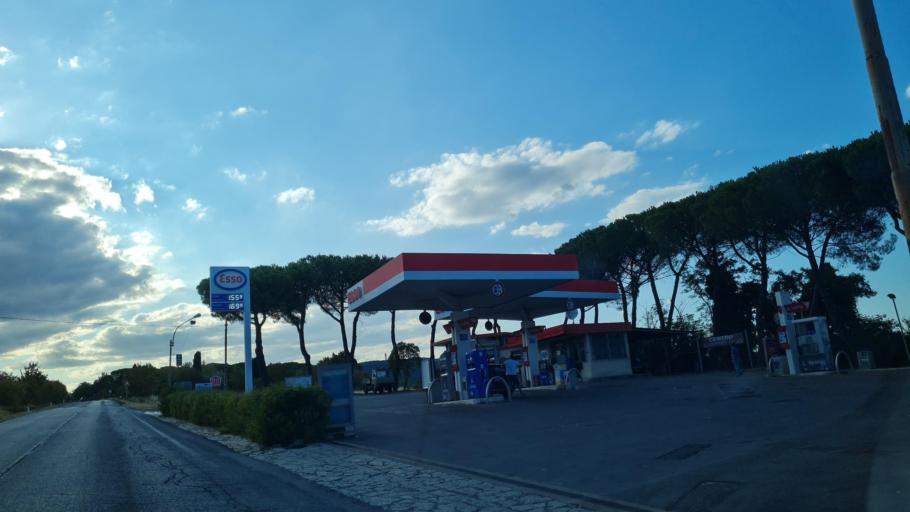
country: IT
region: Tuscany
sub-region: Provincia di Siena
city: Chianciano Terme
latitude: 43.0349
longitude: 11.8409
